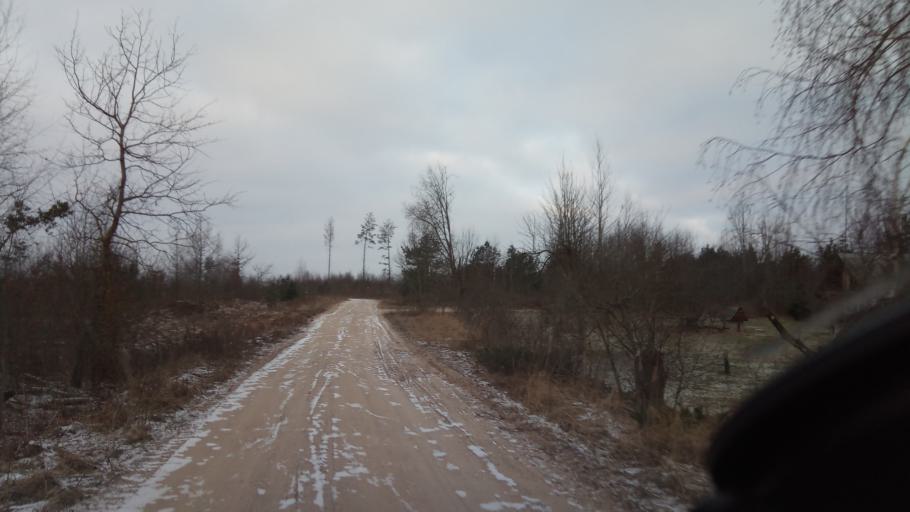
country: LT
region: Alytaus apskritis
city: Varena
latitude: 54.3694
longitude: 24.5437
